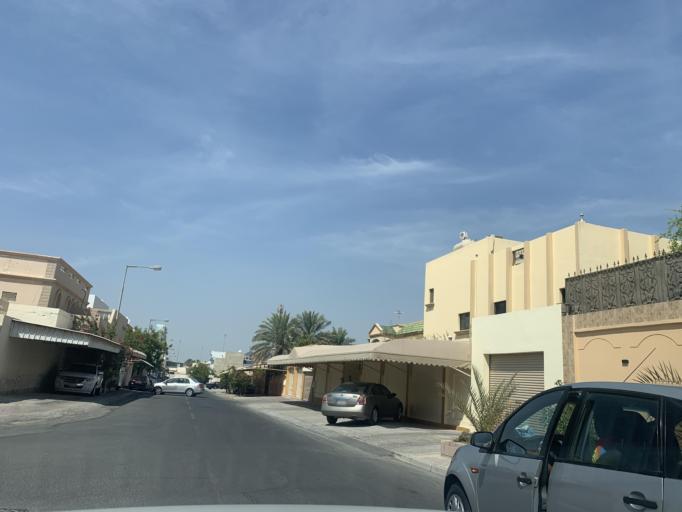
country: BH
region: Central Governorate
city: Madinat Hamad
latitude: 26.1355
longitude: 50.5087
